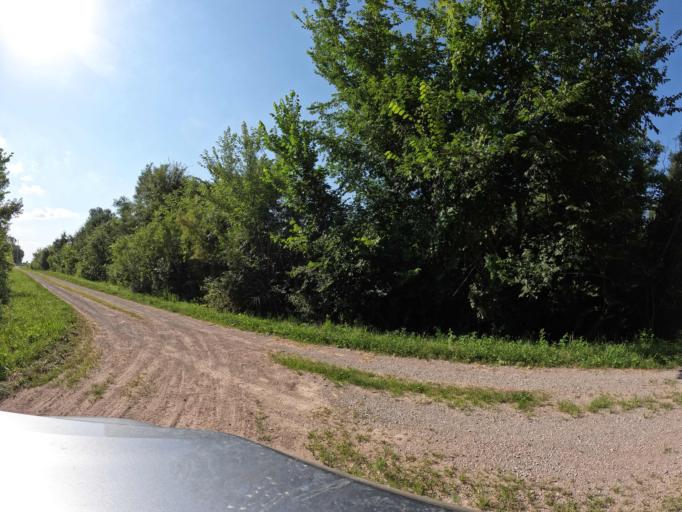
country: US
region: Iowa
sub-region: Appanoose County
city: Centerville
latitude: 40.7202
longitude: -93.0283
